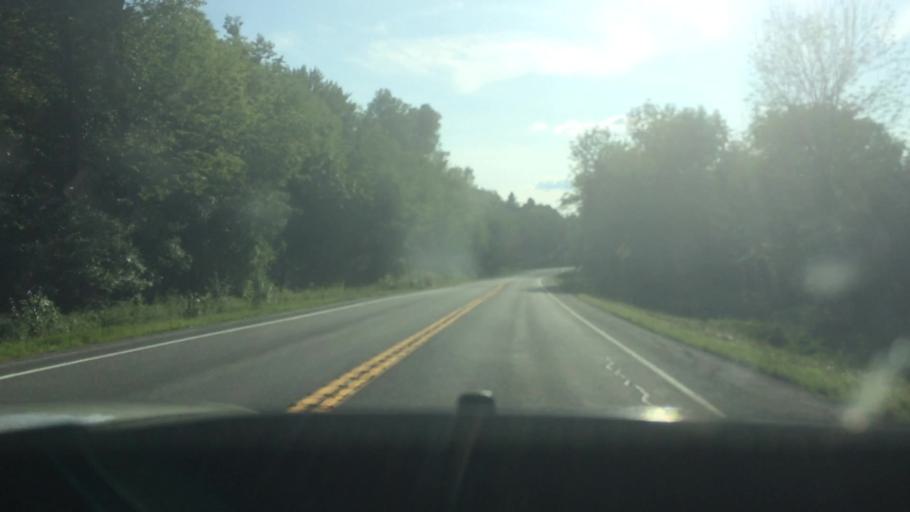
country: US
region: New York
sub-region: St. Lawrence County
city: Potsdam
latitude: 44.6766
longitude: -74.8387
